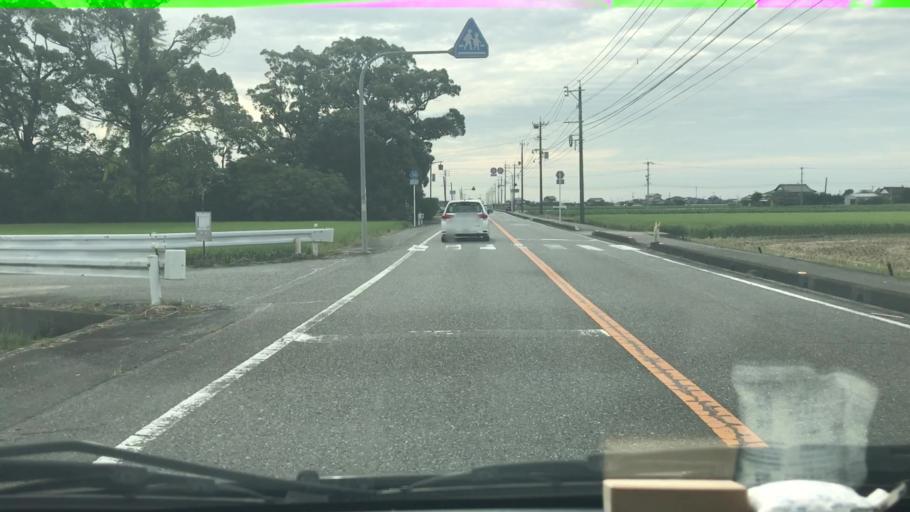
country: JP
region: Saga Prefecture
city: Takeocho-takeo
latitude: 33.2037
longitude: 130.0935
